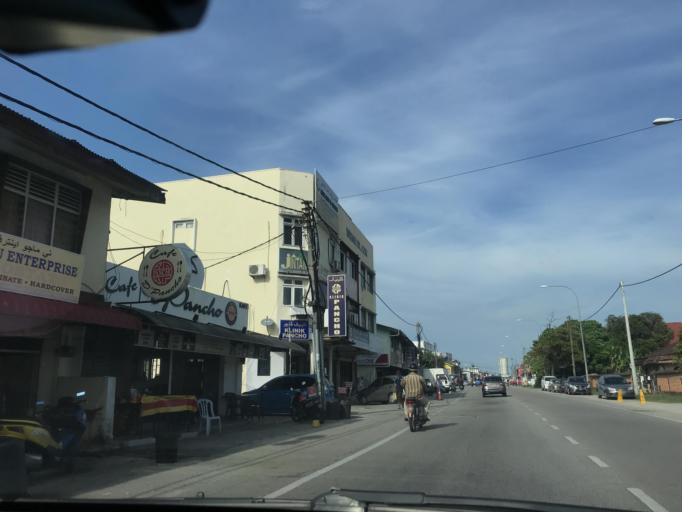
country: MY
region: Kelantan
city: Kota Bharu
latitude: 6.1247
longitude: 102.2496
